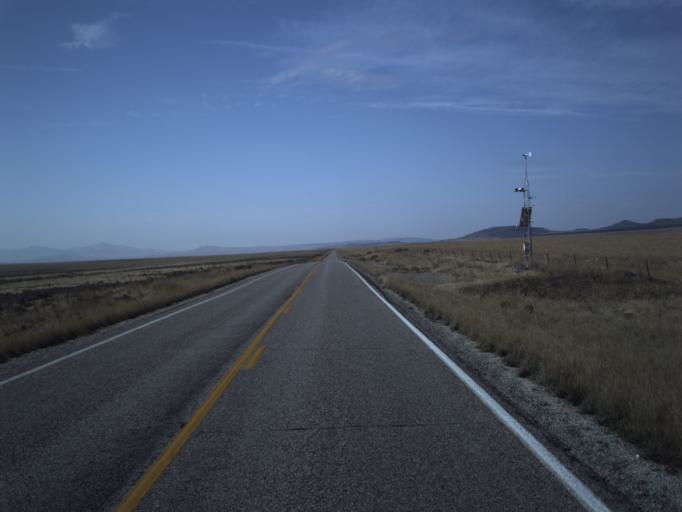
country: US
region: Idaho
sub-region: Oneida County
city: Malad City
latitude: 41.9383
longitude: -113.0854
